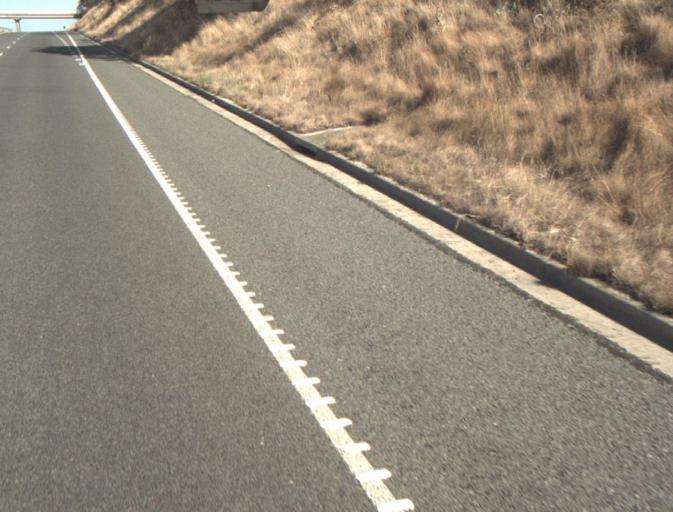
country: AU
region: Tasmania
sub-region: Launceston
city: Mayfield
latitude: -41.3681
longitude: 147.1089
